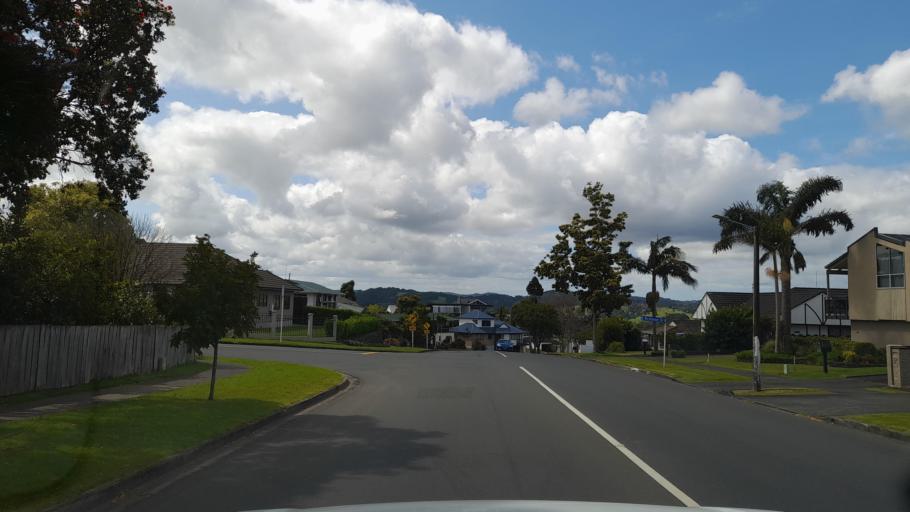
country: NZ
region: Northland
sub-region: Whangarei
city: Whangarei
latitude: -35.6878
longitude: 174.2968
